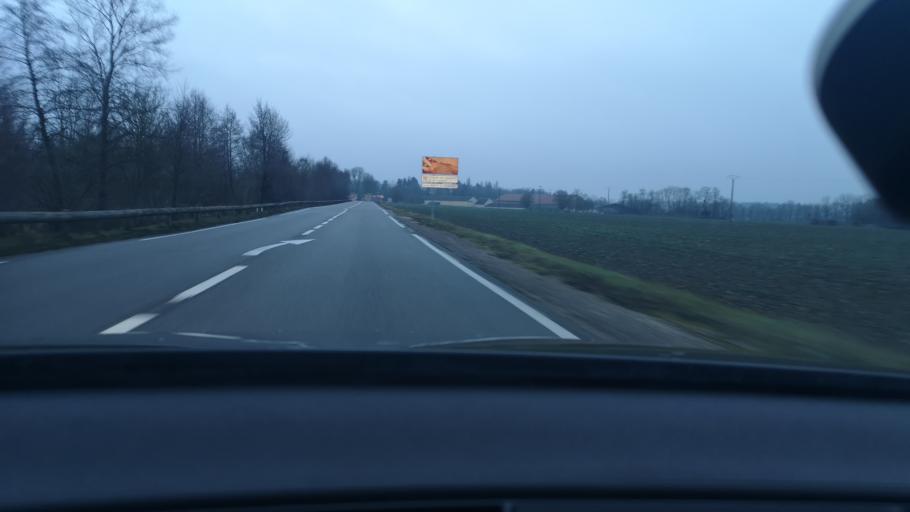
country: FR
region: Bourgogne
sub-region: Departement de la Cote-d'Or
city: Aiserey
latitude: 47.1348
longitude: 5.0931
